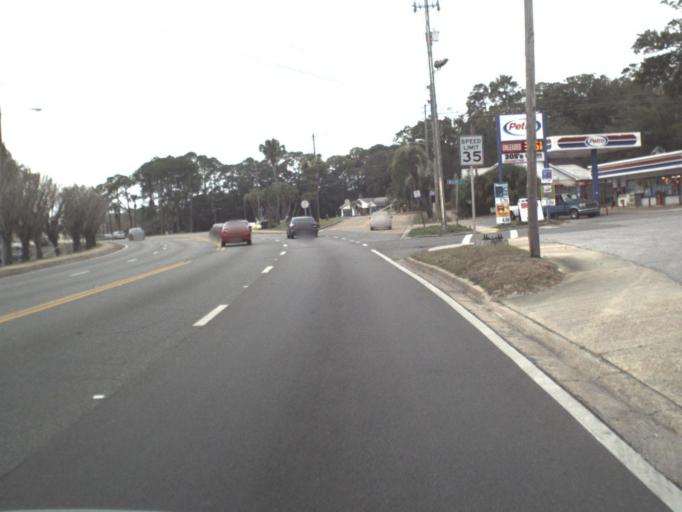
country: US
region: Florida
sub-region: Bay County
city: Panama City
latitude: 30.1572
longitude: -85.6404
